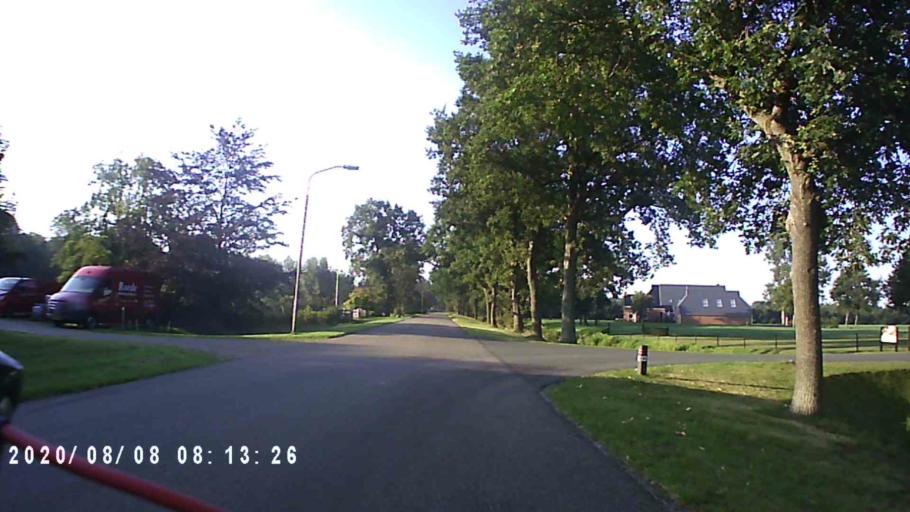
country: NL
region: Groningen
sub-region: Gemeente Leek
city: Leek
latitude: 53.1001
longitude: 6.3403
